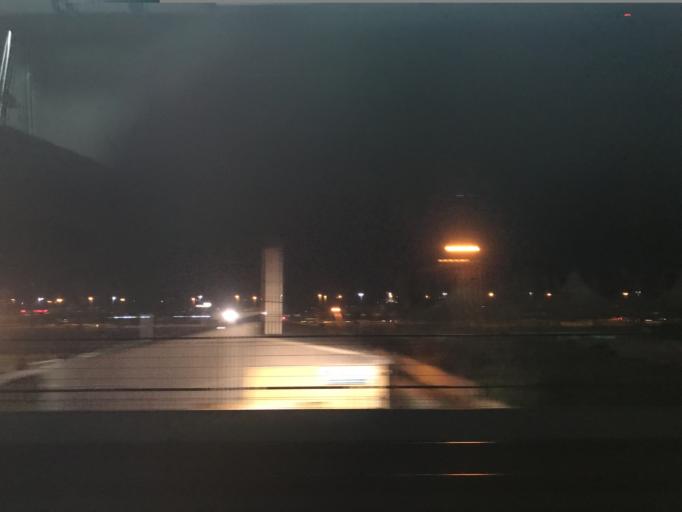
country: TR
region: Istanbul
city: Pendik
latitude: 40.8748
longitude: 29.2484
